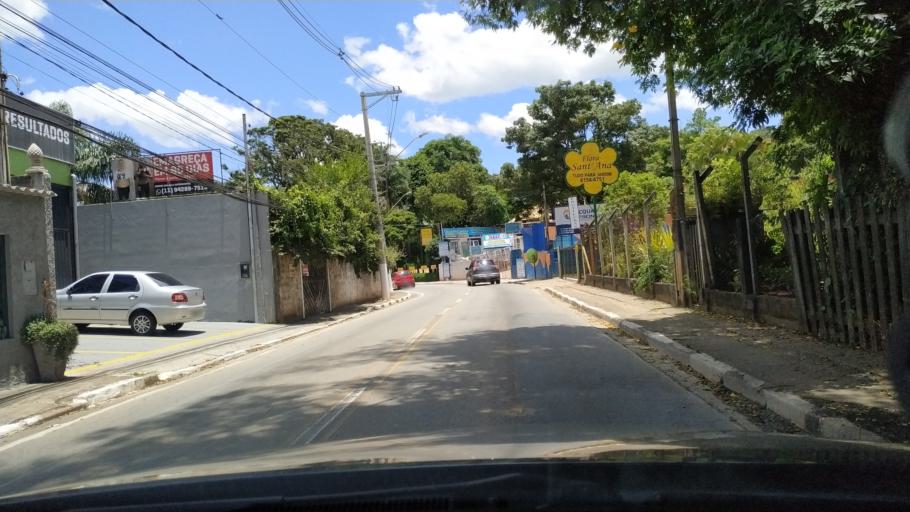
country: BR
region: Sao Paulo
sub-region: Santana De Parnaiba
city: Santana de Parnaiba
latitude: -23.4406
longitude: -46.9119
